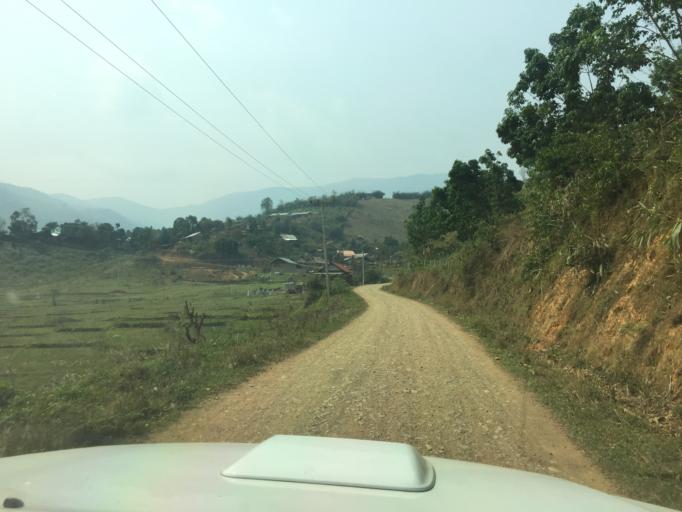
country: TH
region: Phayao
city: Phu Sang
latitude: 19.5698
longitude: 100.5254
